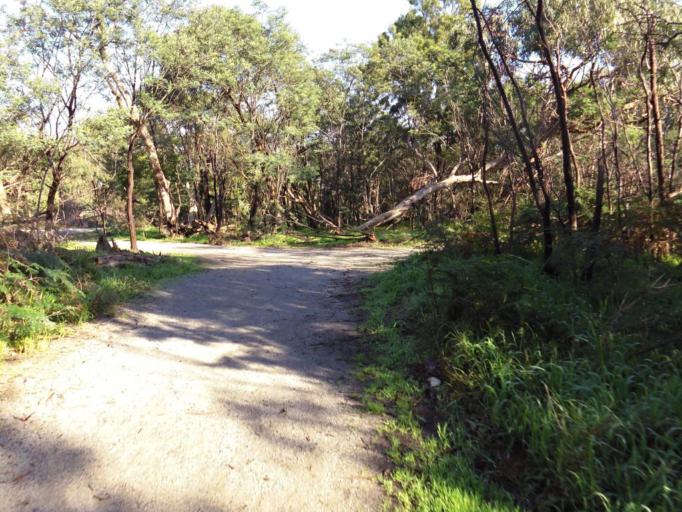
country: AU
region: Victoria
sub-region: Kingston
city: Dingley Village
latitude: -37.9954
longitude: 145.1302
